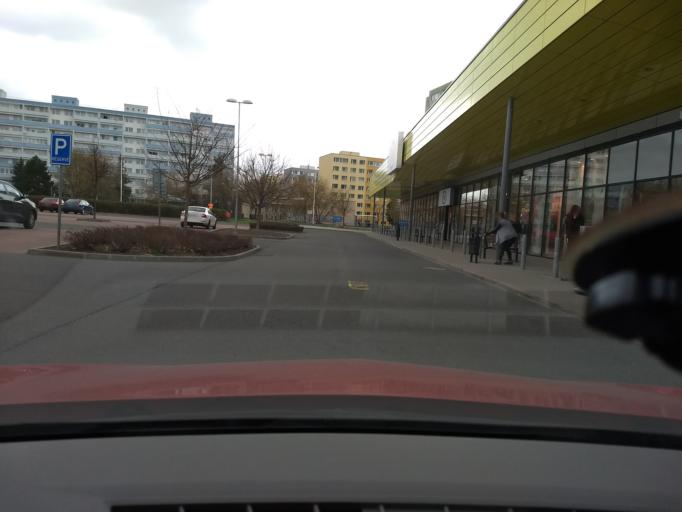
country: CZ
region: Central Bohemia
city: Kladno
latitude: 50.1264
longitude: 14.1237
